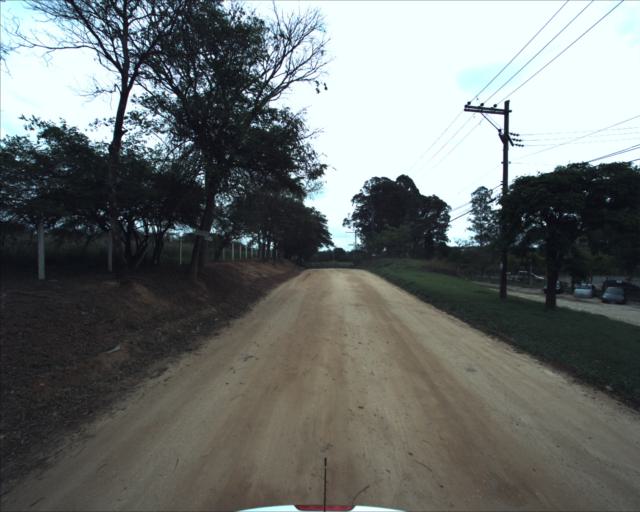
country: BR
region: Sao Paulo
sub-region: Sorocaba
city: Sorocaba
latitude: -23.4603
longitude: -47.3906
